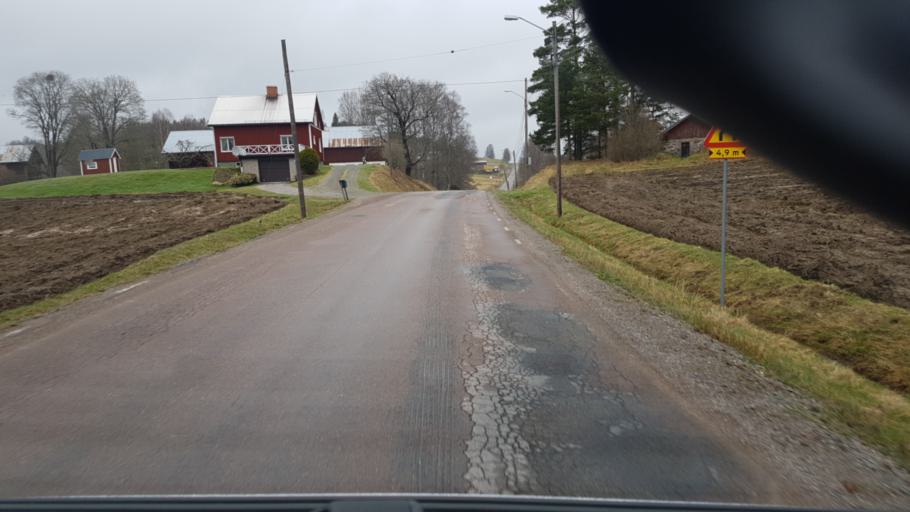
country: SE
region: Vaermland
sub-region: Eda Kommun
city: Charlottenberg
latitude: 59.9303
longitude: 12.5209
